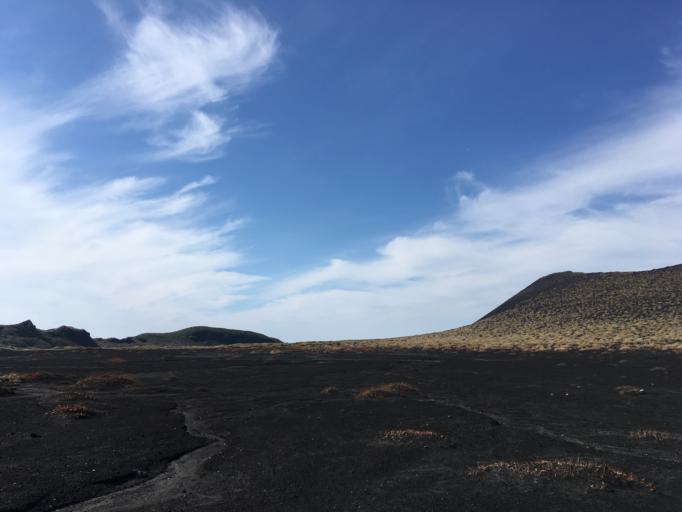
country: JP
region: Shizuoka
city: Ito
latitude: 34.7250
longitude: 139.4072
